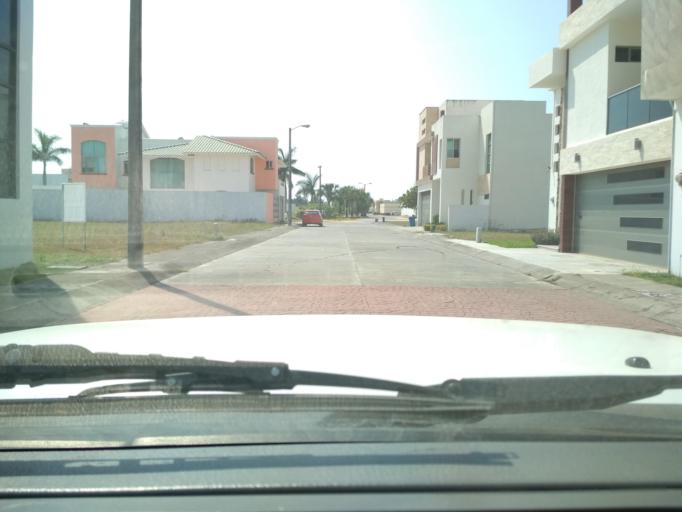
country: MX
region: Veracruz
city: Boca del Rio
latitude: 19.1031
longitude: -96.1213
